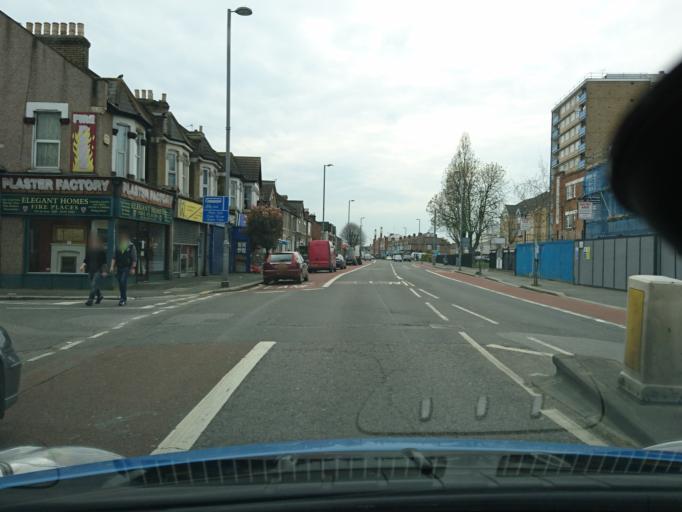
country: GB
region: England
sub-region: Greater London
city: Walthamstow
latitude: 51.5727
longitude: -0.0174
